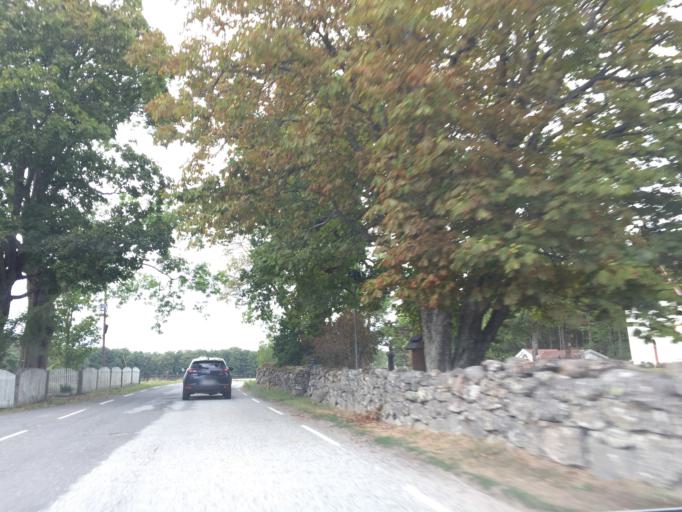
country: NO
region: Ostfold
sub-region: Hvaler
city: Skjaerhalden
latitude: 59.0319
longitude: 11.0251
